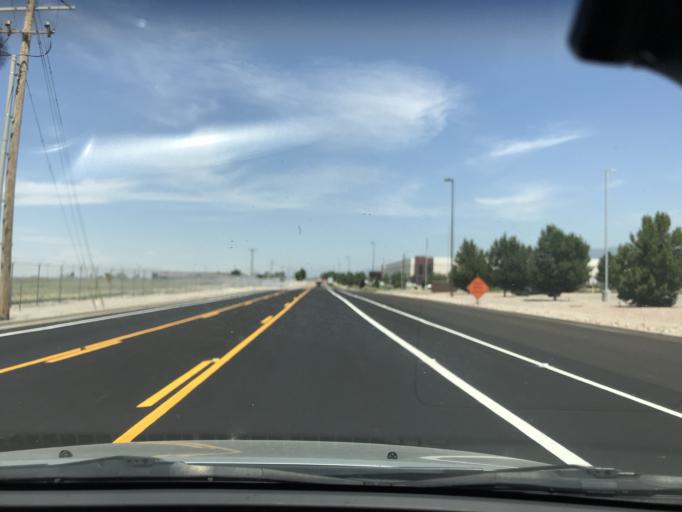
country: US
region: Utah
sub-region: Davis County
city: North Salt Lake
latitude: 40.8041
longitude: -111.9535
